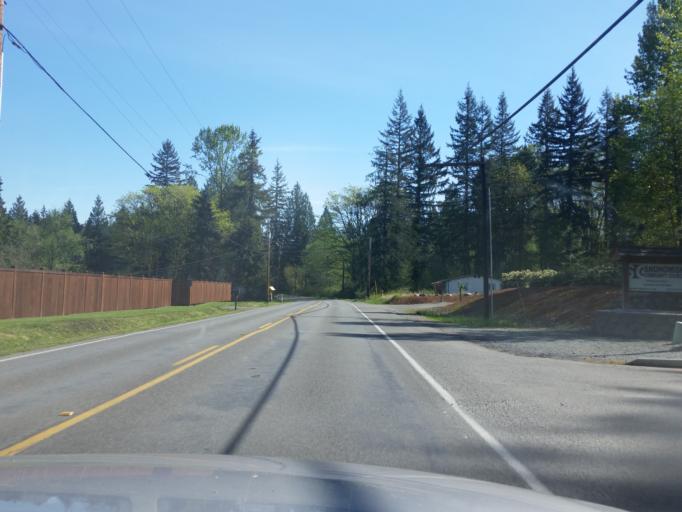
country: US
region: Washington
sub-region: Snohomish County
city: Machias
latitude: 47.9604
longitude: -122.0482
